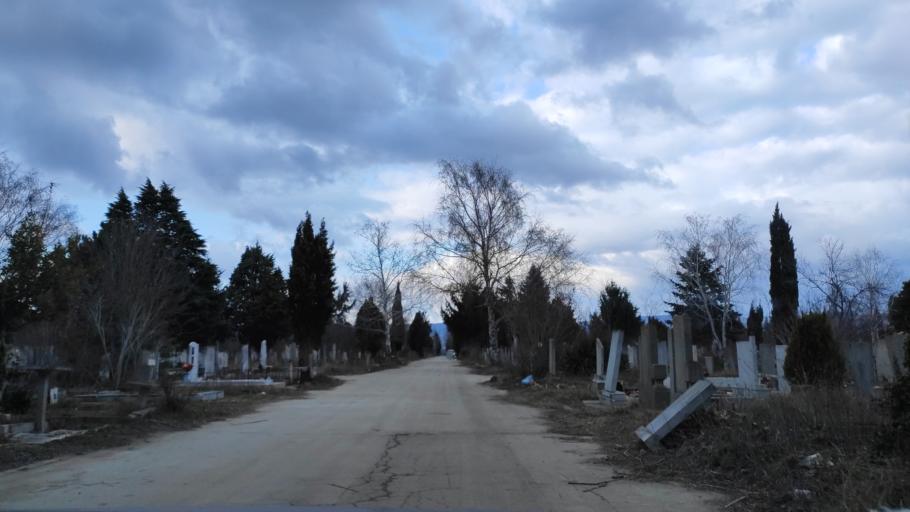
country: BG
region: Varna
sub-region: Obshtina Aksakovo
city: Aksakovo
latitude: 43.2193
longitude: 27.8090
